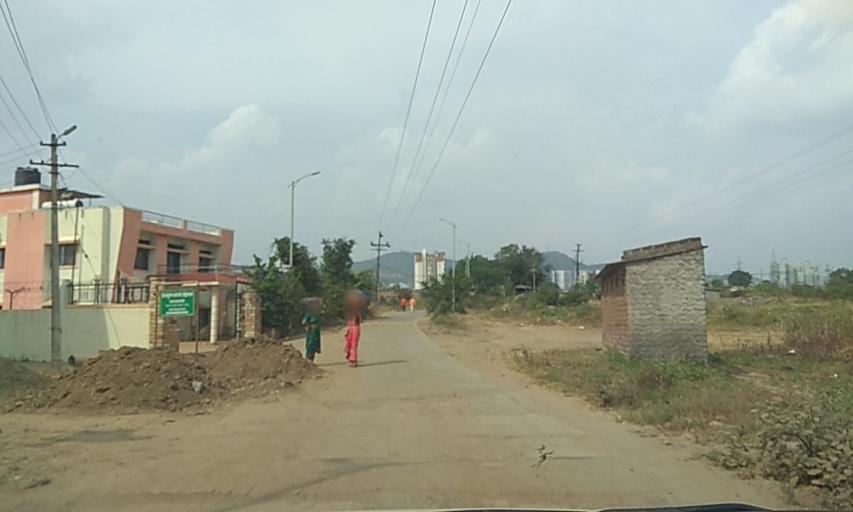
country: IN
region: Maharashtra
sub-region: Pune Division
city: Pimpri
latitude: 18.5832
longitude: 73.7061
